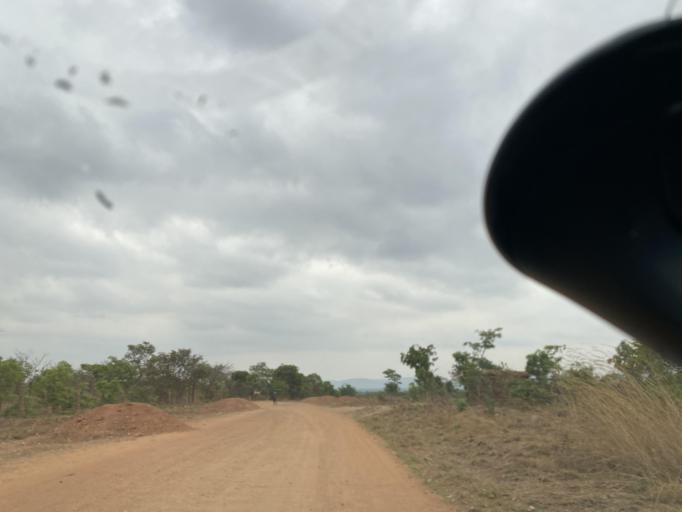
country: ZM
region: Lusaka
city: Chongwe
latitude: -15.2573
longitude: 28.7299
